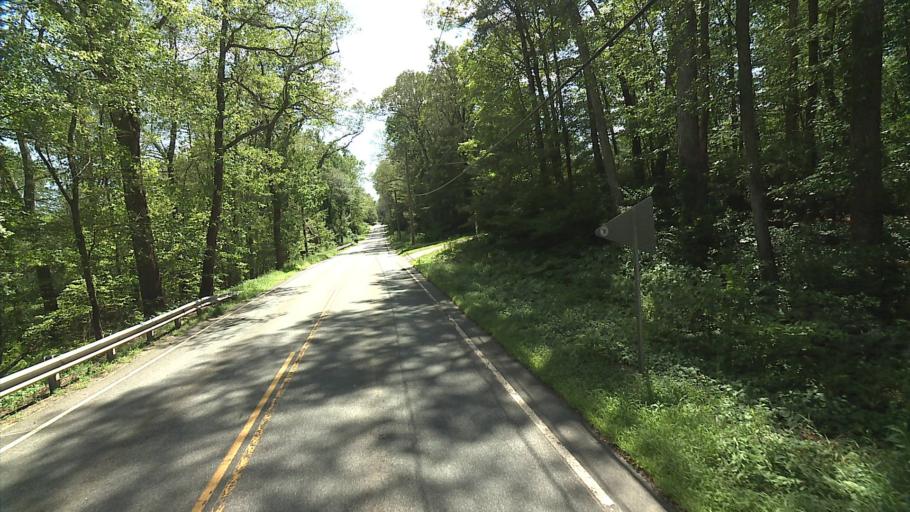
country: US
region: Connecticut
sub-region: Windham County
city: South Woodstock
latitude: 41.8824
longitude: -71.9753
